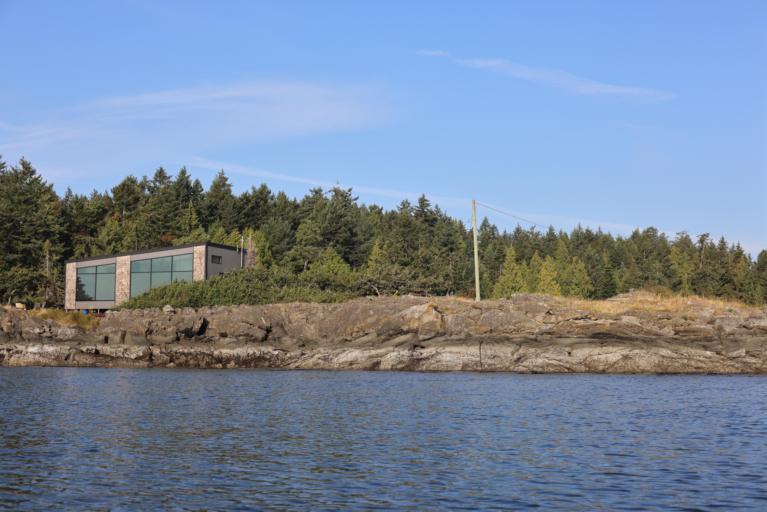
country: CA
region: British Columbia
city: North Saanich
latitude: 48.6795
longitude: -123.3967
